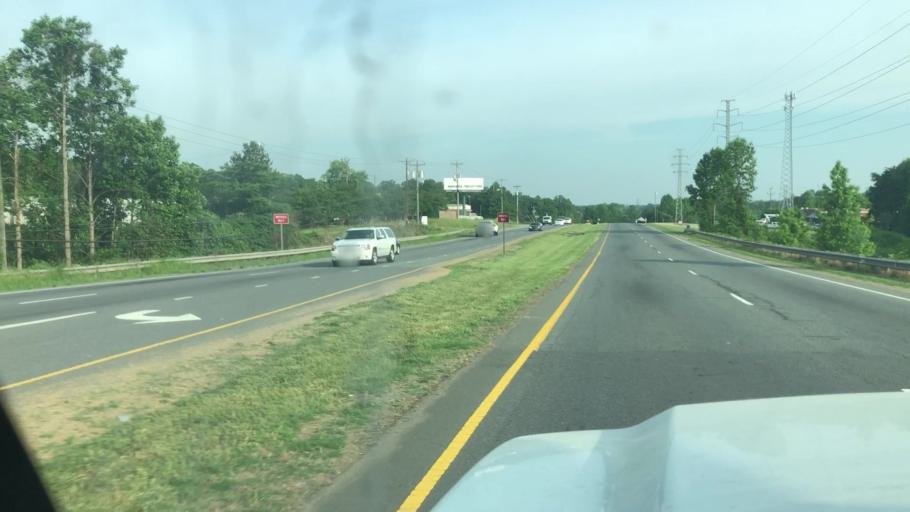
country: US
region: North Carolina
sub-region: Mecklenburg County
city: Charlotte
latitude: 35.2918
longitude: -80.9141
